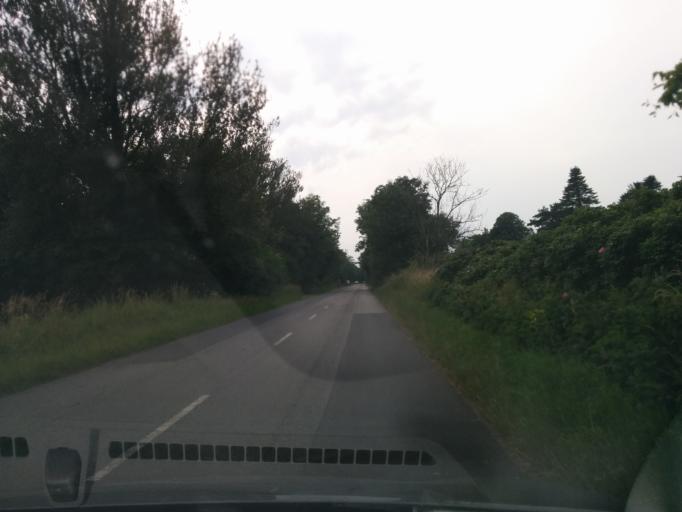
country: DK
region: Central Jutland
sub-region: Arhus Kommune
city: Beder
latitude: 56.0401
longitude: 10.2536
